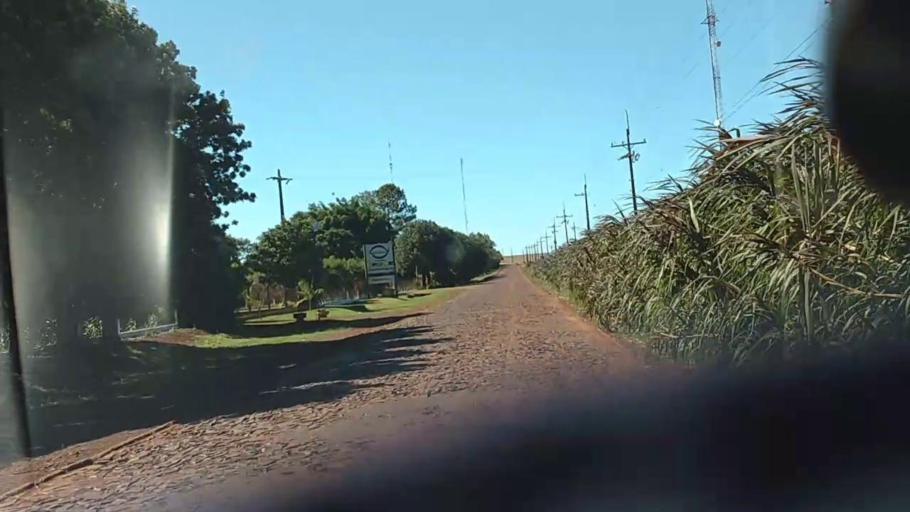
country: PY
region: Alto Parana
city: Naranjal
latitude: -25.9766
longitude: -55.1670
